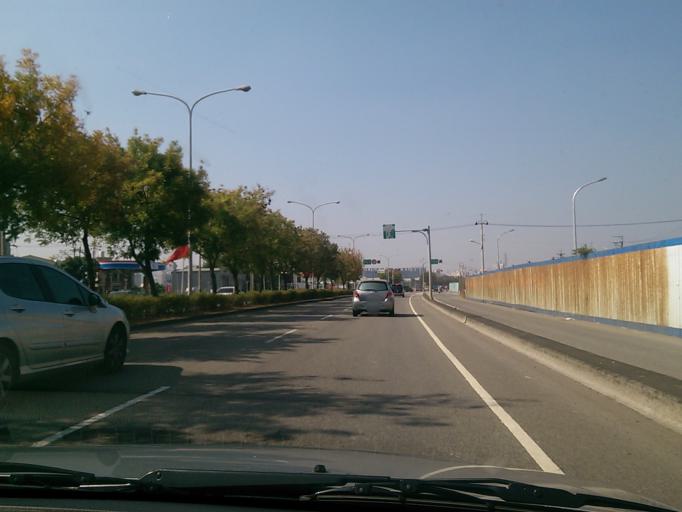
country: TW
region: Taiwan
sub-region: Taichung City
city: Taichung
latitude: 24.1308
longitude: 120.6265
